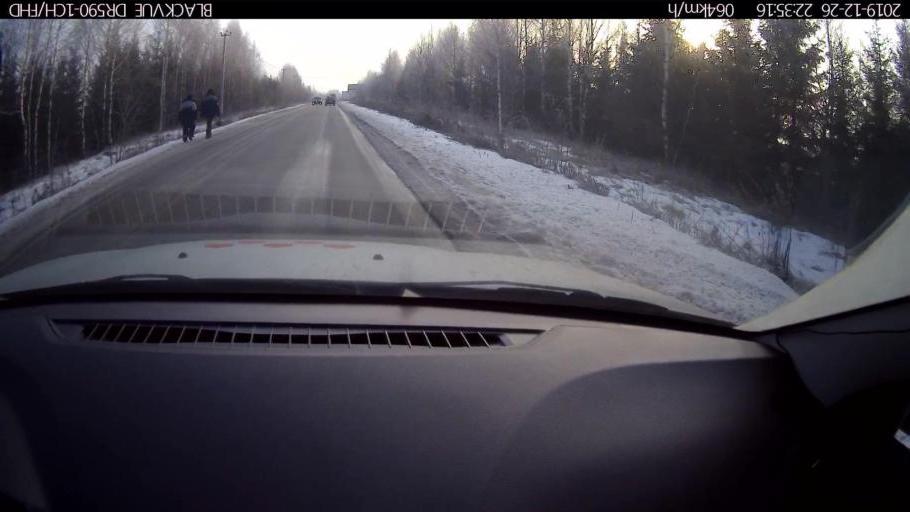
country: RU
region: Nizjnij Novgorod
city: Burevestnik
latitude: 56.1487
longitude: 43.7182
